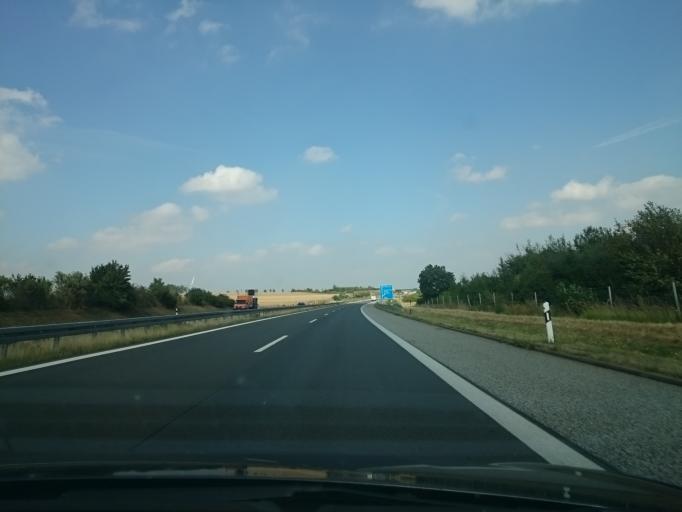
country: DE
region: Brandenburg
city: Grunow
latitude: 53.3000
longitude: 13.9868
